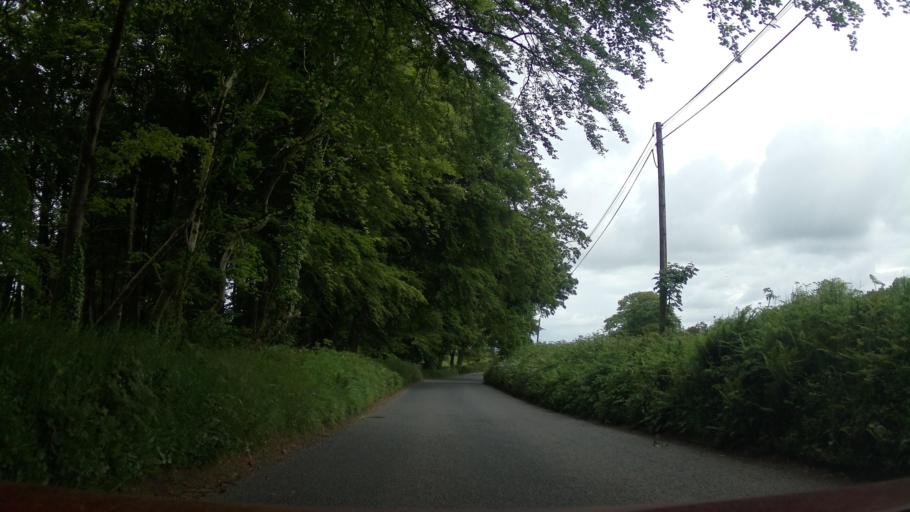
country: GB
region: England
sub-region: Devon
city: Totnes
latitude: 50.3527
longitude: -3.6612
